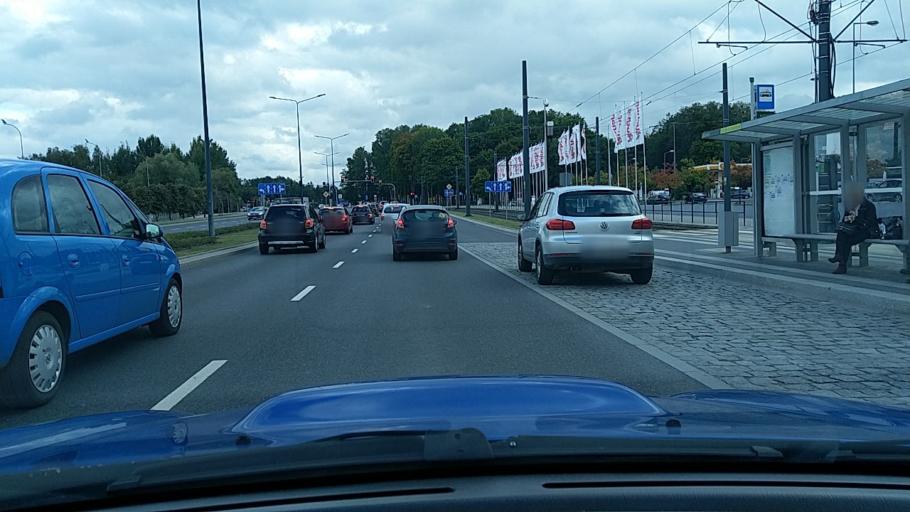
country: PL
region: Warmian-Masurian Voivodeship
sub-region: Powiat olsztynski
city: Olsztyn
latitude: 53.7514
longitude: 20.4861
